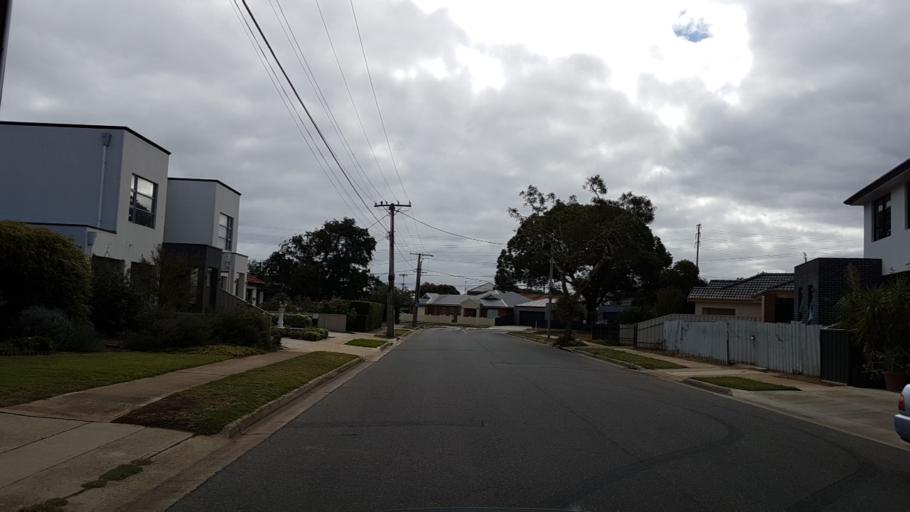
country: AU
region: South Australia
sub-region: Charles Sturt
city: Seaton
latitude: -34.9076
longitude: 138.5204
